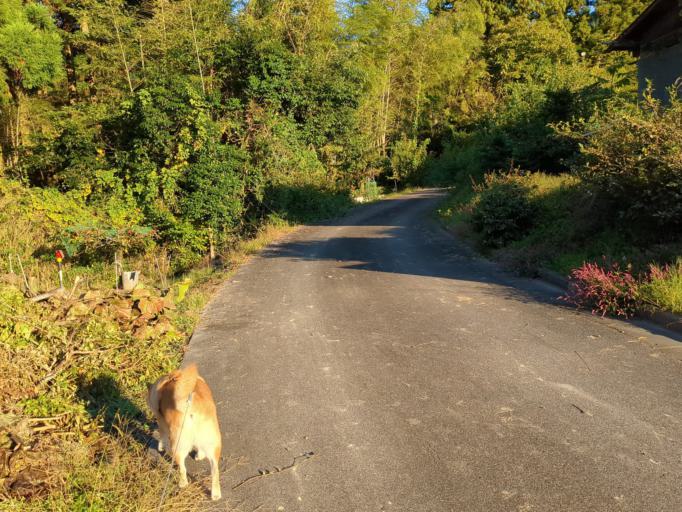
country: JP
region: Gifu
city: Tarui
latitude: 35.4018
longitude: 136.5273
